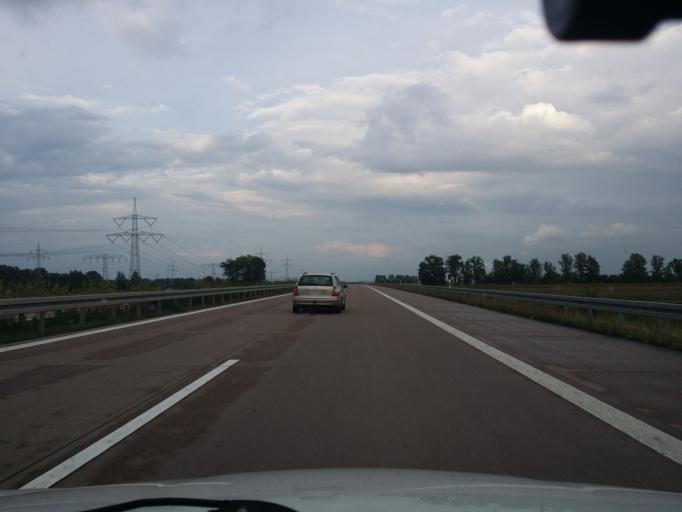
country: DE
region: Saxony-Anhalt
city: Schafstadt
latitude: 51.4031
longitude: 11.7940
